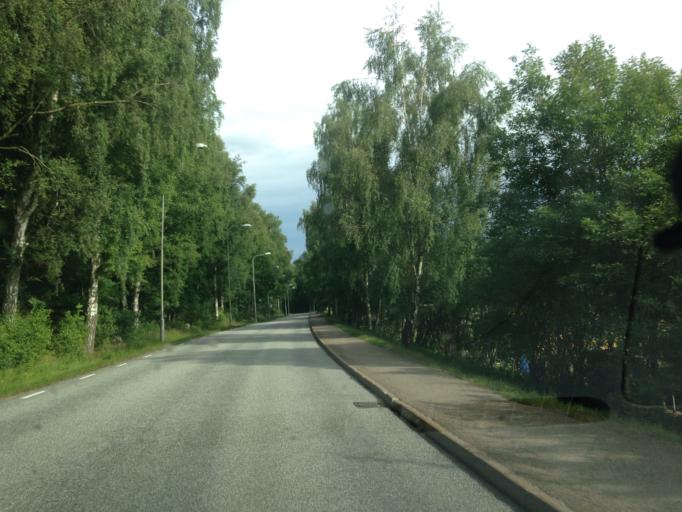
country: SE
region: Vaestra Goetaland
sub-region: Goteborg
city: Goeteborg
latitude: 57.7628
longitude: 11.9785
